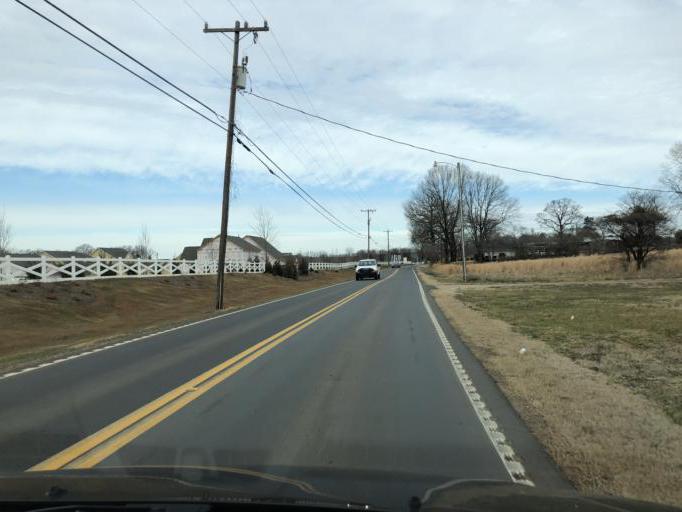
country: US
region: South Carolina
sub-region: Greenville County
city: Five Forks
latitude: 34.8704
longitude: -82.1994
